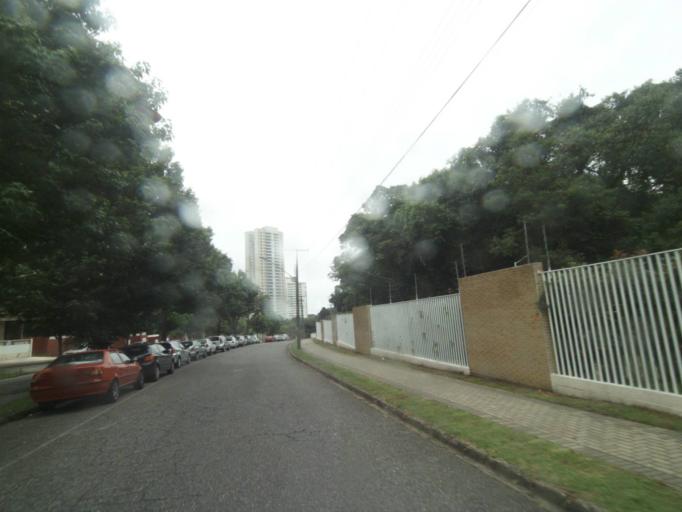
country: BR
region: Parana
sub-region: Curitiba
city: Curitiba
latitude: -25.4415
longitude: -49.3483
